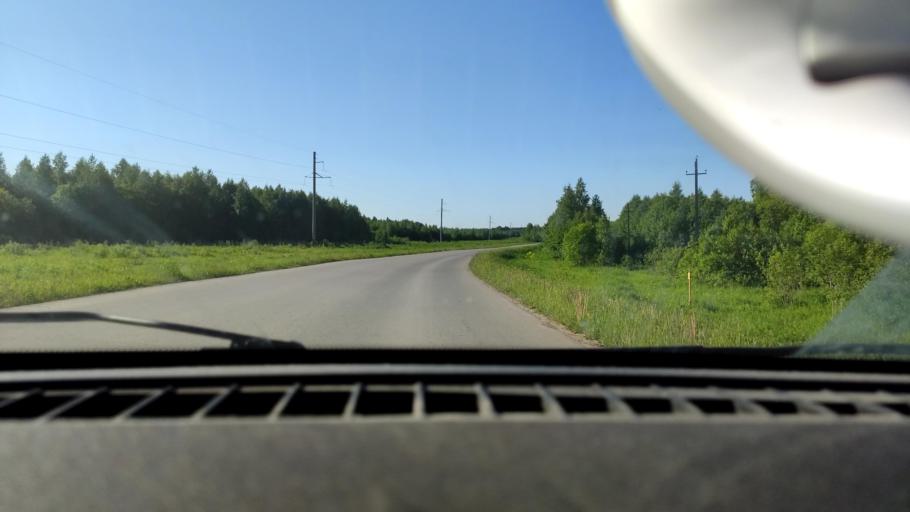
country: RU
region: Perm
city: Polazna
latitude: 58.2074
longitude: 56.5297
